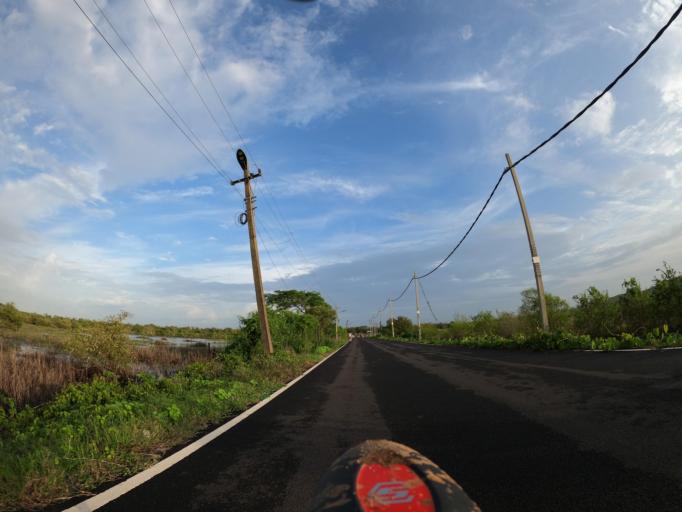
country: IN
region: Goa
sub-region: North Goa
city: Serula
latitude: 15.5301
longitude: 73.8577
